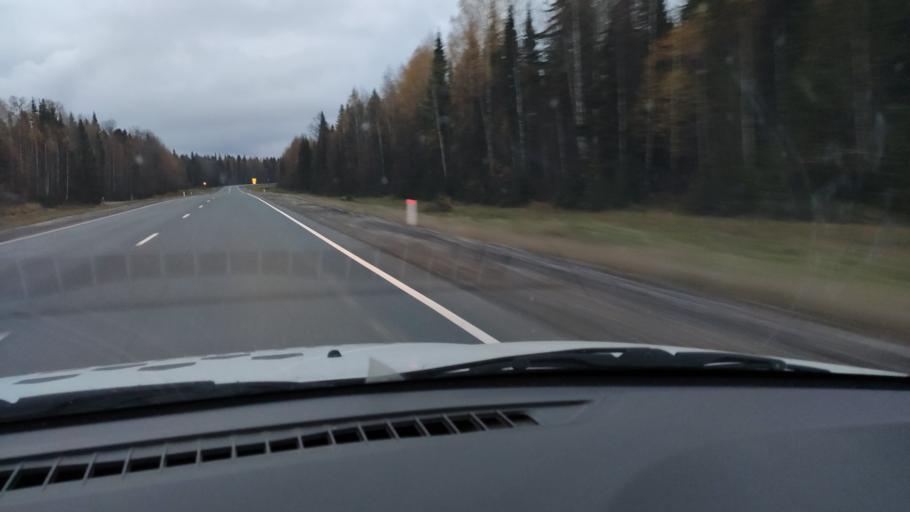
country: RU
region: Kirov
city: Kostino
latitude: 58.8552
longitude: 53.0980
